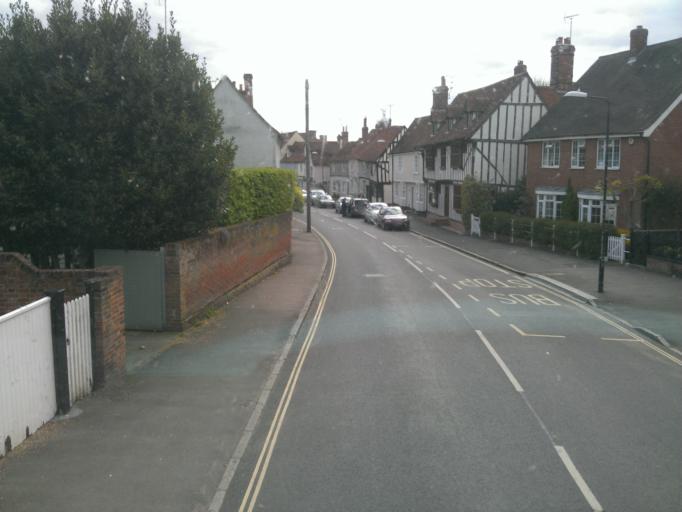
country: GB
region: England
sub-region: Essex
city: Coggeshall
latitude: 51.8732
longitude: 0.6896
